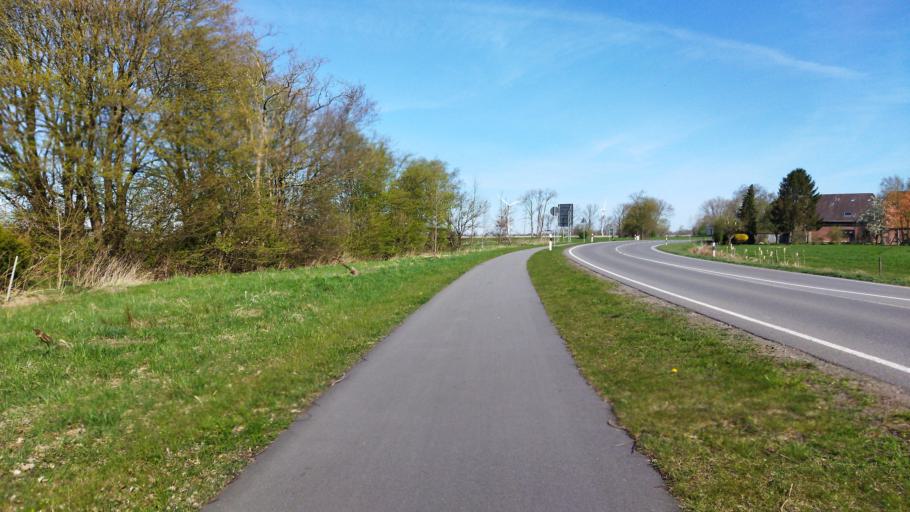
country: DE
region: Lower Saxony
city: Elsfleth
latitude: 53.2038
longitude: 8.4436
